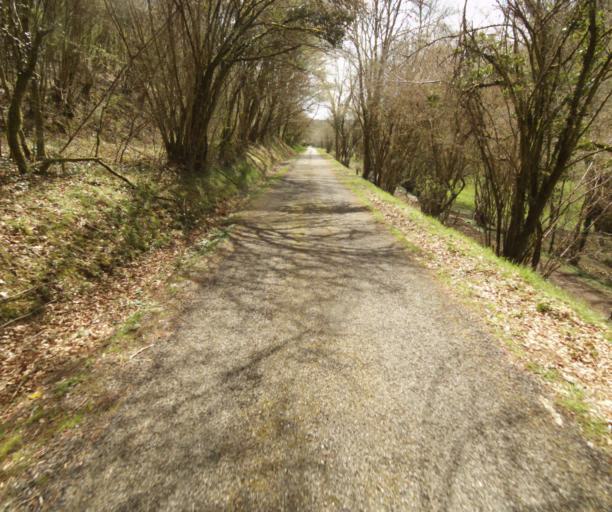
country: FR
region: Limousin
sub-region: Departement de la Correze
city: Argentat
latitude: 45.1822
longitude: 1.8767
